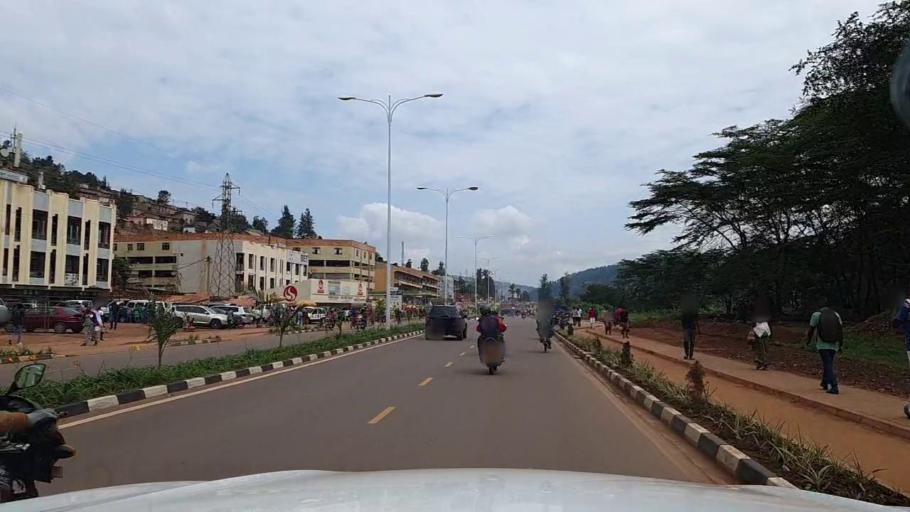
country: RW
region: Kigali
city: Kigali
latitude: -1.9375
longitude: 30.0444
